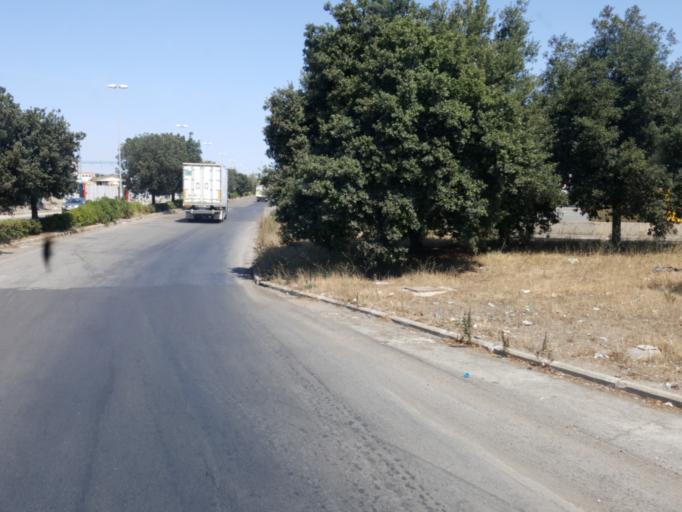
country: IT
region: Latium
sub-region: Citta metropolitana di Roma Capitale
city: Aurelia
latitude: 42.1163
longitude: 11.7791
